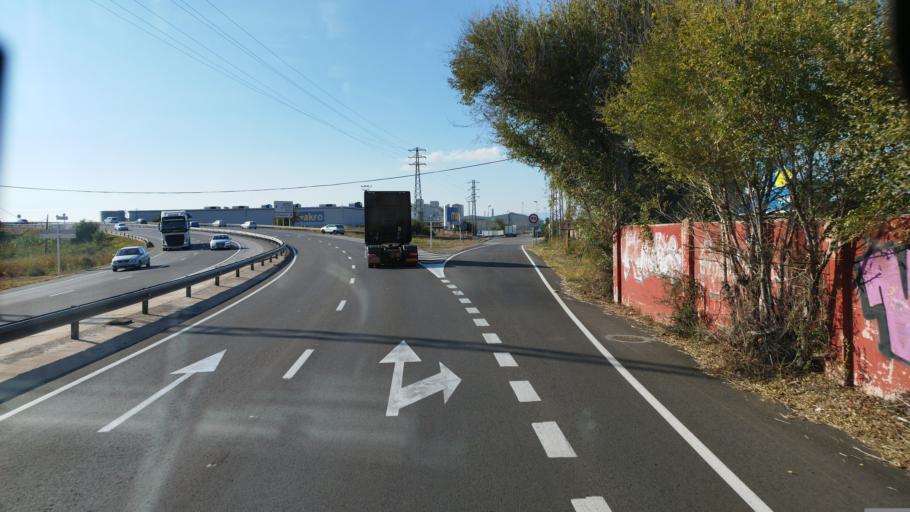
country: ES
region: Catalonia
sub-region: Provincia de Tarragona
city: Tarragona
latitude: 41.1129
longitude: 1.2129
